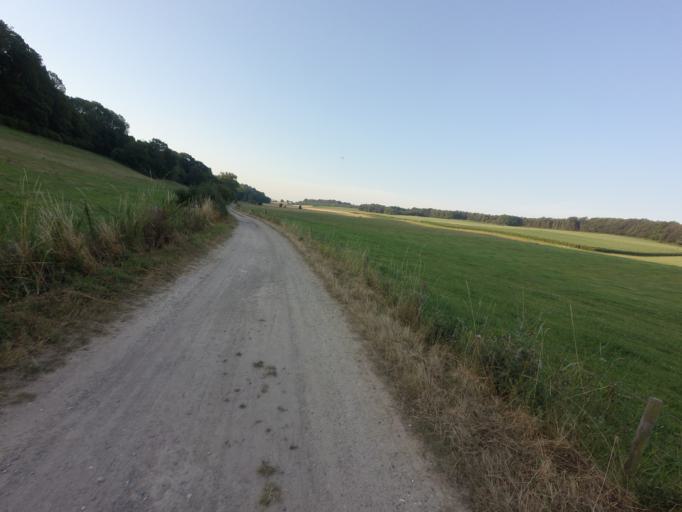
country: NL
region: Limburg
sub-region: Valkenburg aan de Geul
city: Schin op Geul
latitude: 50.7964
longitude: 5.8734
